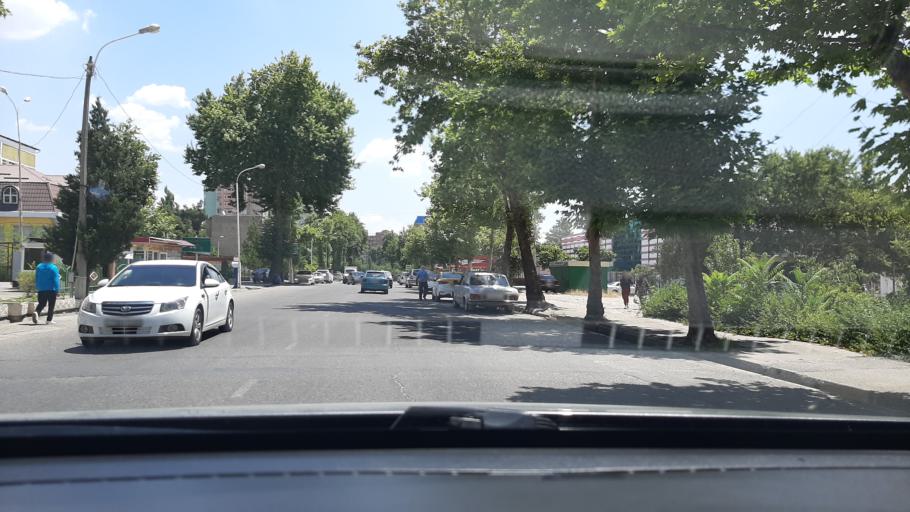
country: TJ
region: Dushanbe
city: Dushanbe
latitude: 38.5330
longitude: 68.7649
